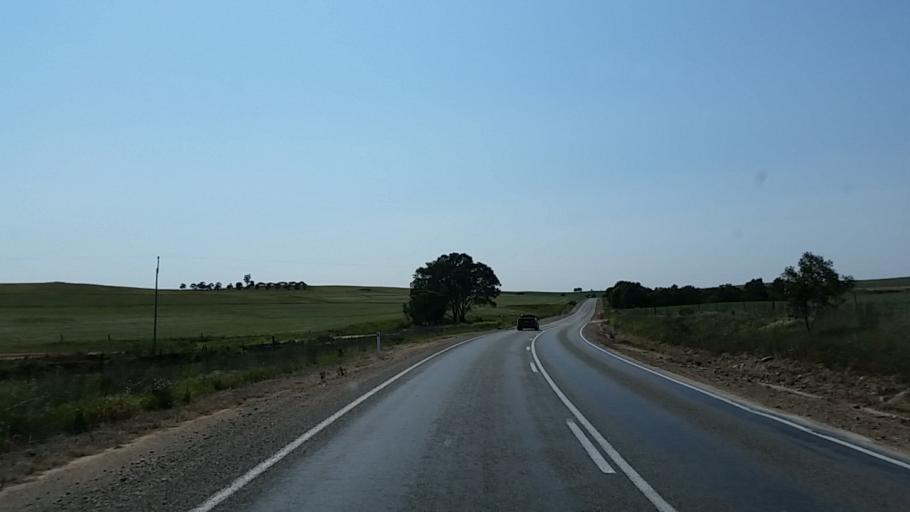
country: AU
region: South Australia
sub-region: Northern Areas
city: Jamestown
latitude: -33.2083
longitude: 138.4288
